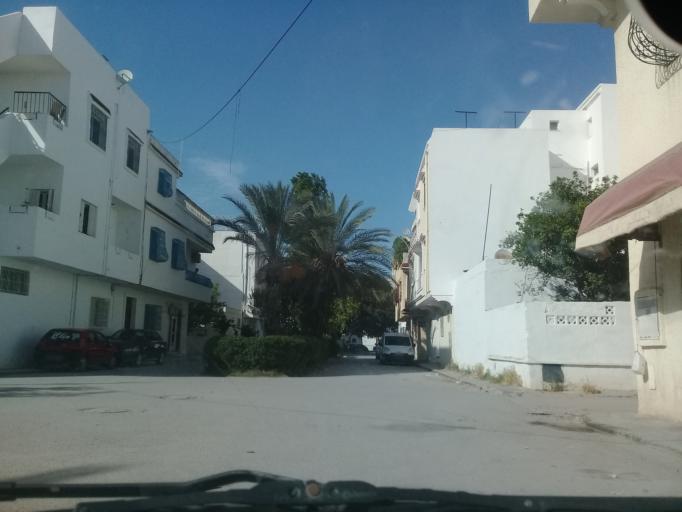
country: TN
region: Ariana
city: Ariana
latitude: 36.8315
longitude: 10.1939
